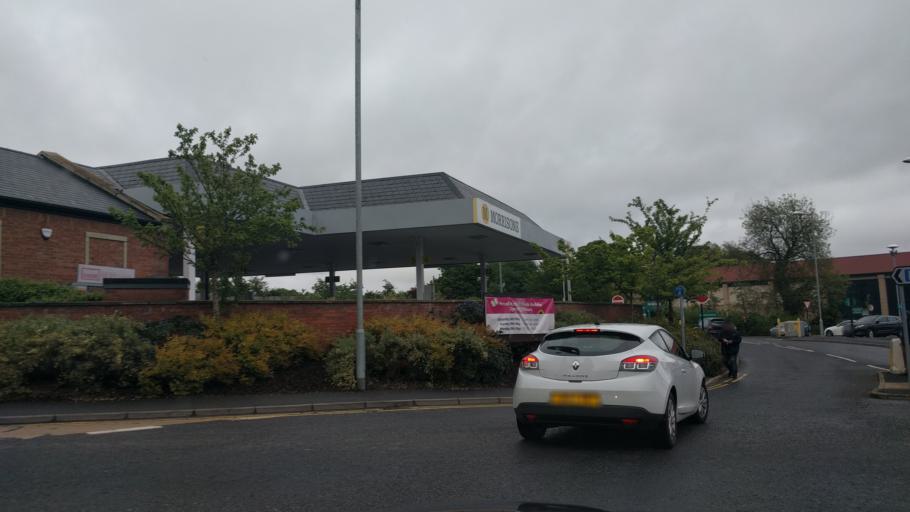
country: GB
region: England
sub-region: Northumberland
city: Morpeth
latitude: 55.1697
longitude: -1.6861
